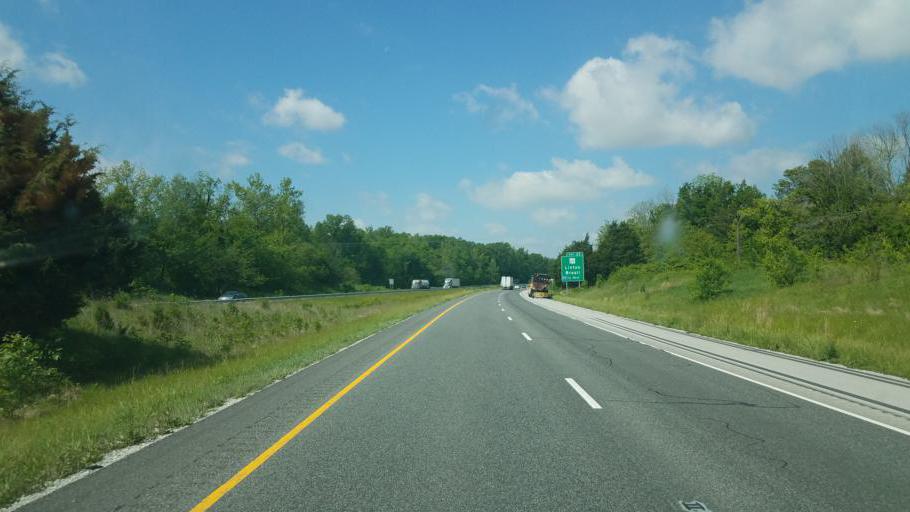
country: US
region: Indiana
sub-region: Clay County
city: Brazil
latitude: 39.4515
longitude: -87.1074
